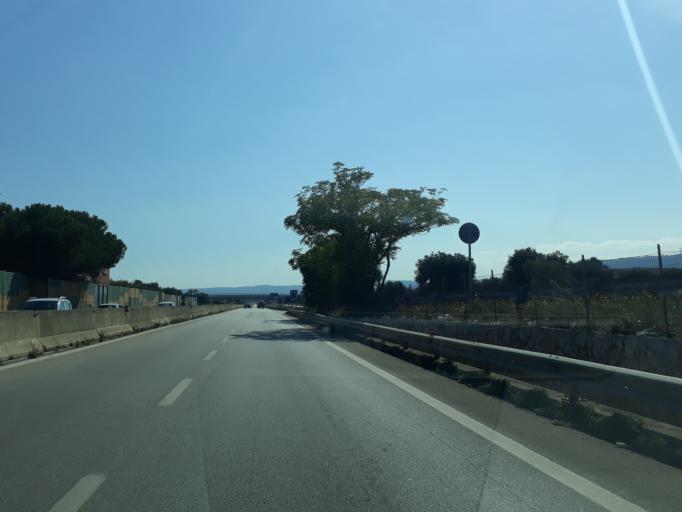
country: IT
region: Apulia
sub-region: Provincia di Brindisi
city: Fasano
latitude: 40.8772
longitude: 17.3398
